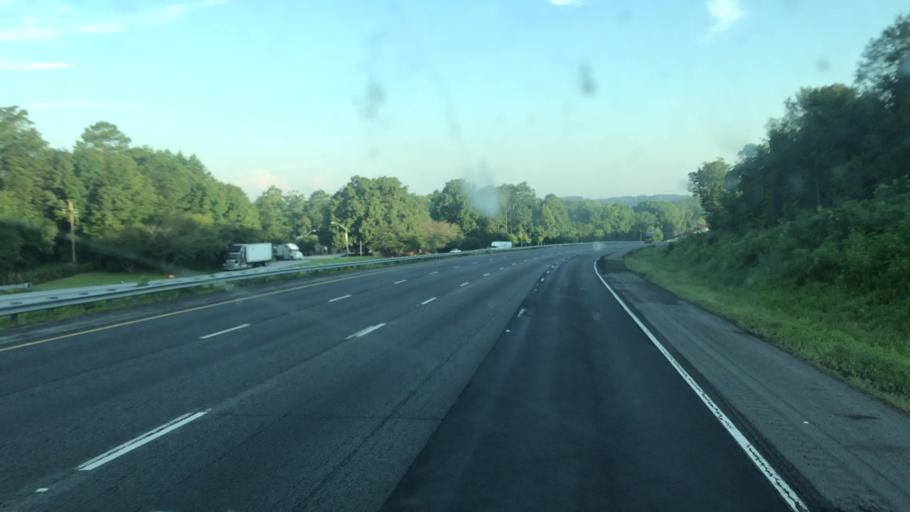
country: US
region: Georgia
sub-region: Monroe County
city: Forsyth
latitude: 32.9706
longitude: -83.8250
